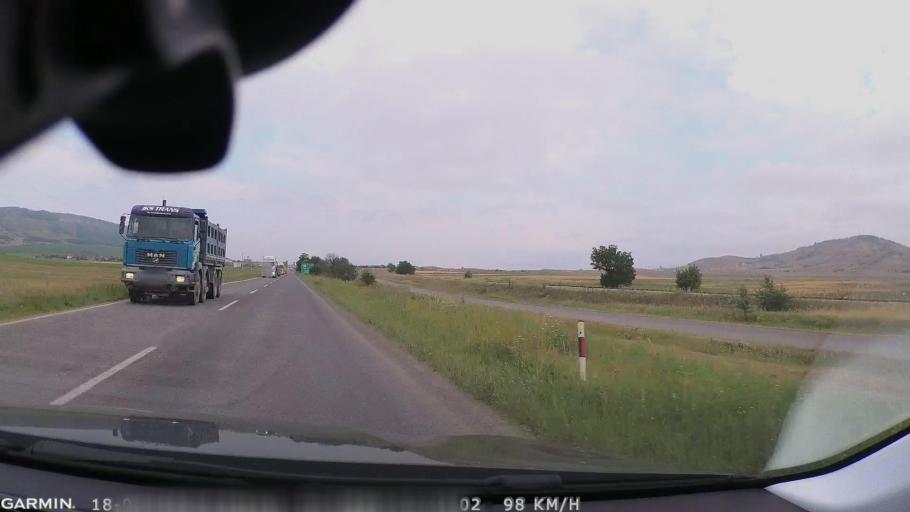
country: MK
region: Stip
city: Shtip
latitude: 41.7690
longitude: 22.1500
